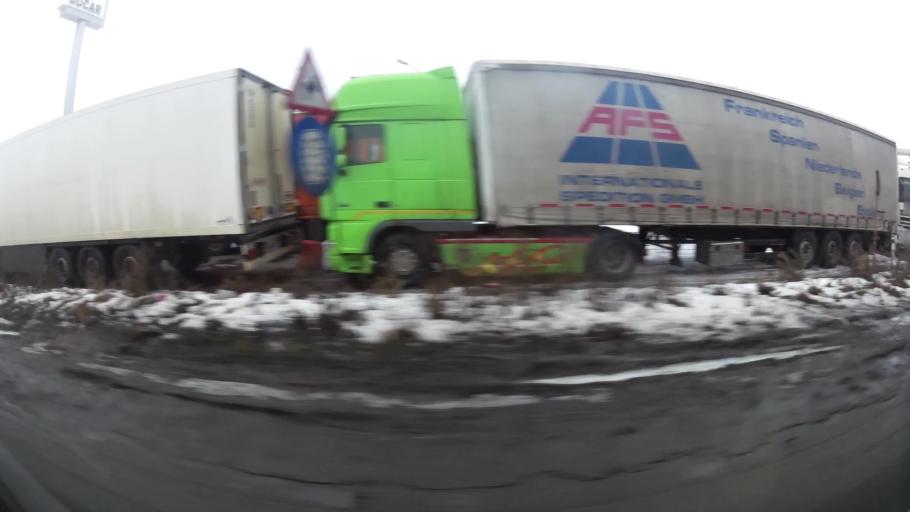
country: RO
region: Ilfov
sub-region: Comuna Chiajna
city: Chiajna
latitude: 44.4341
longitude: 25.9672
